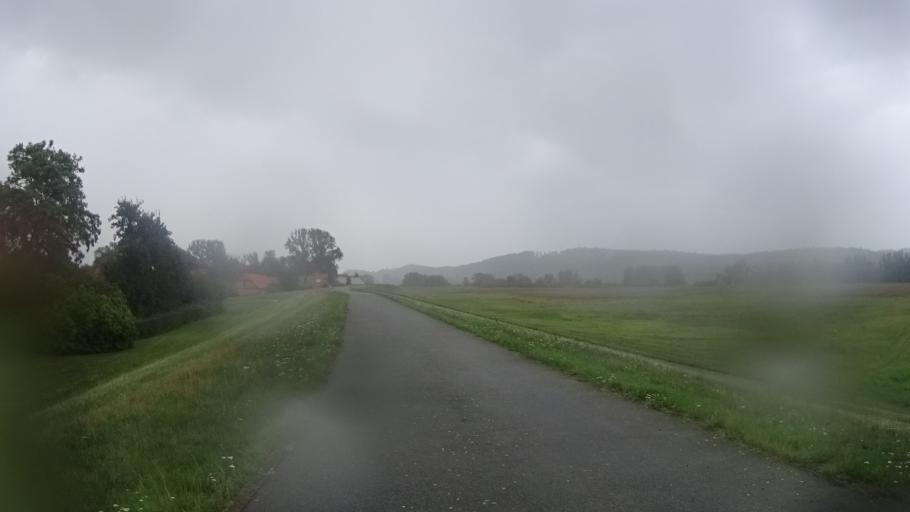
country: DE
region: Lower Saxony
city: Hitzacker
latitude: 53.1727
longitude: 11.0312
